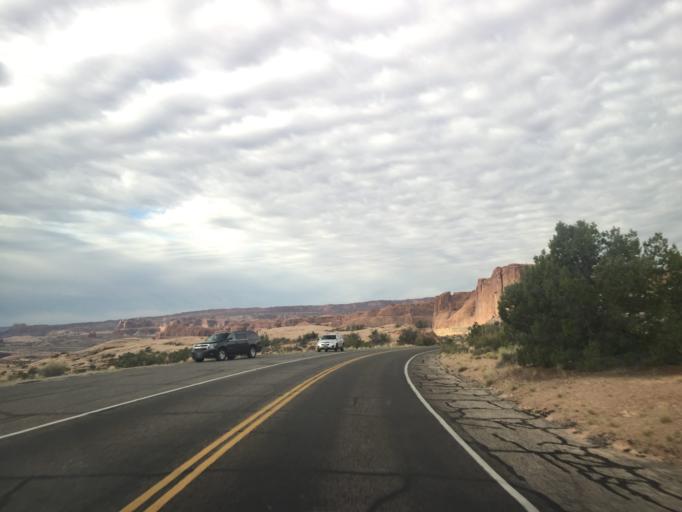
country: US
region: Utah
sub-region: Grand County
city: Moab
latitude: 38.6827
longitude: -109.5826
